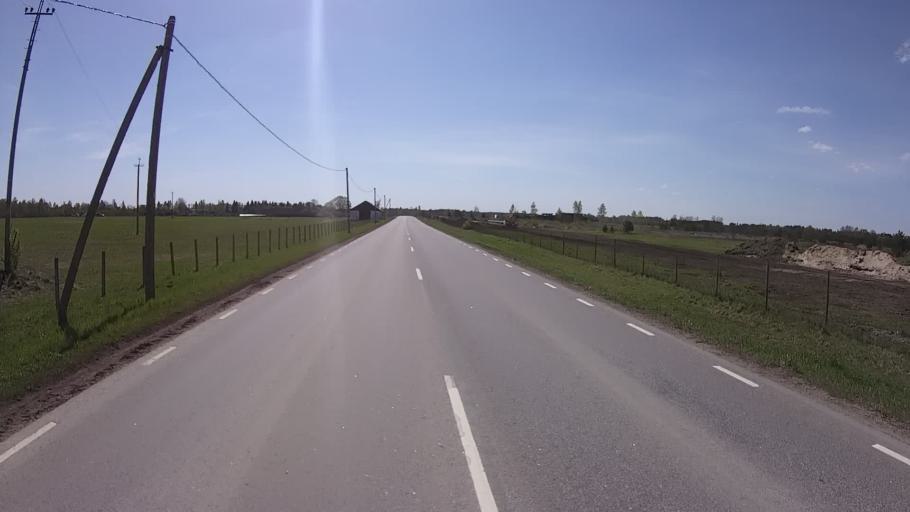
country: EE
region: Harju
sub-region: Keila linn
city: Keila
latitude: 59.3214
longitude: 24.3231
